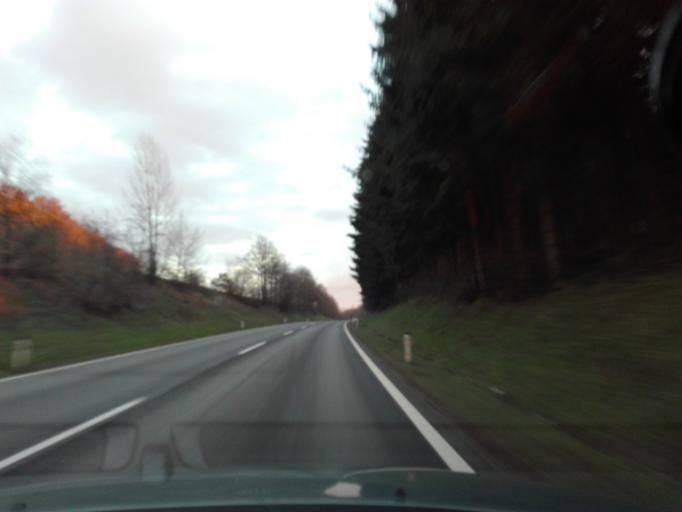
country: AT
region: Upper Austria
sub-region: Politischer Bezirk Perg
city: Bad Kreuzen
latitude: 48.2149
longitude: 14.7464
